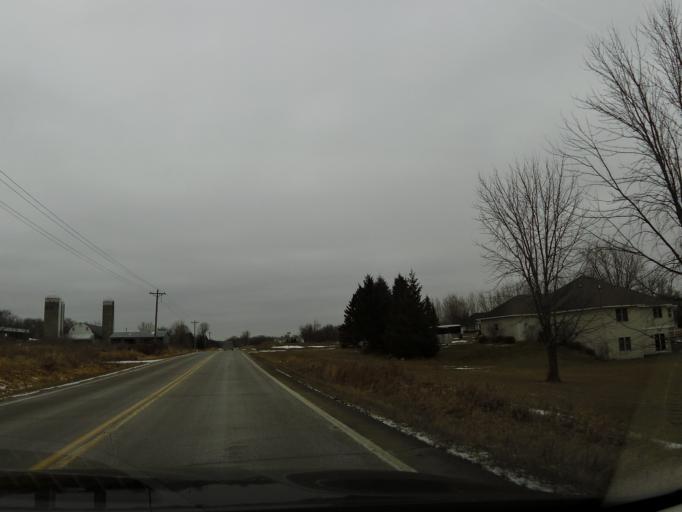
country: US
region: Minnesota
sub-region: Hennepin County
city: Independence
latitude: 45.0254
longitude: -93.7275
